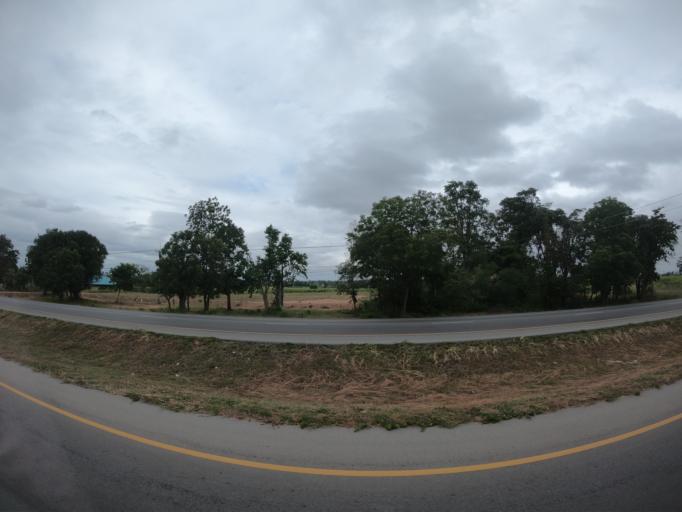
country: TH
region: Khon Kaen
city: Ban Phai
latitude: 16.0443
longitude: 102.8481
